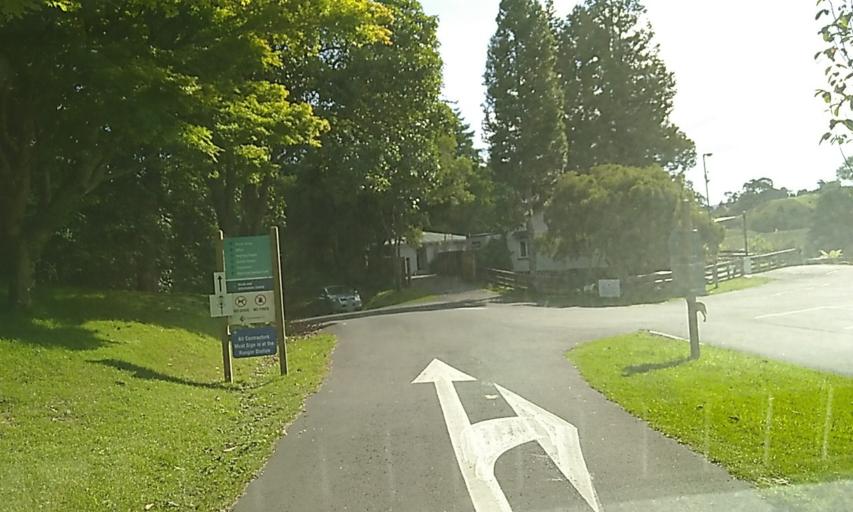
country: NZ
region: Bay of Plenty
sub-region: Tauranga City
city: Tauranga
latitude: -37.8095
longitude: 176.0450
